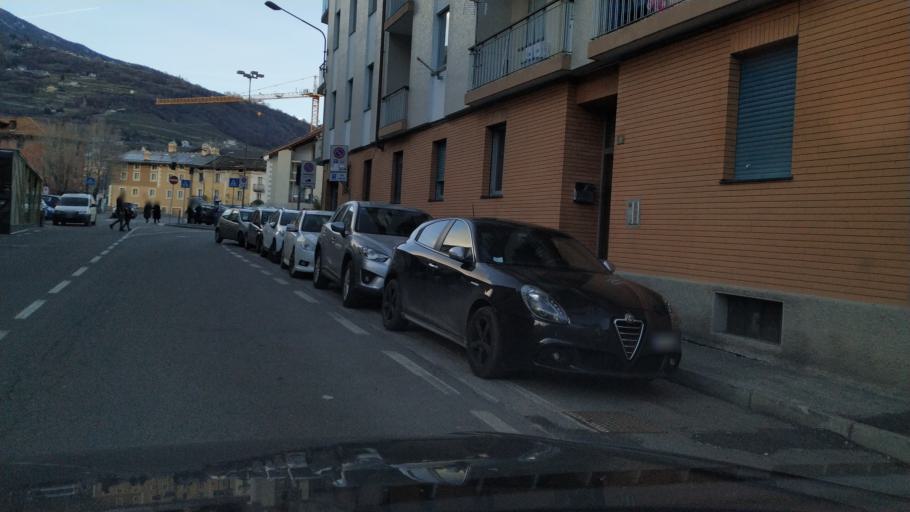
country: IT
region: Aosta Valley
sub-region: Valle d'Aosta
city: Aosta
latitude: 45.7389
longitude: 7.3304
